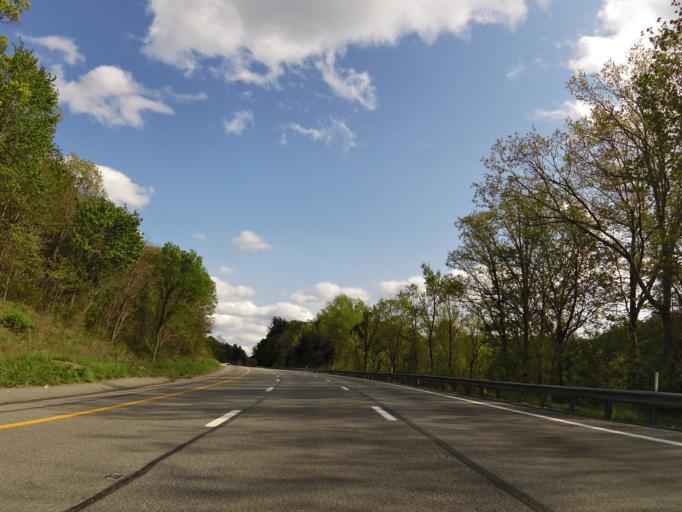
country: US
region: West Virginia
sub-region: Raleigh County
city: Shady Spring
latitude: 37.6527
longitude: -81.1136
